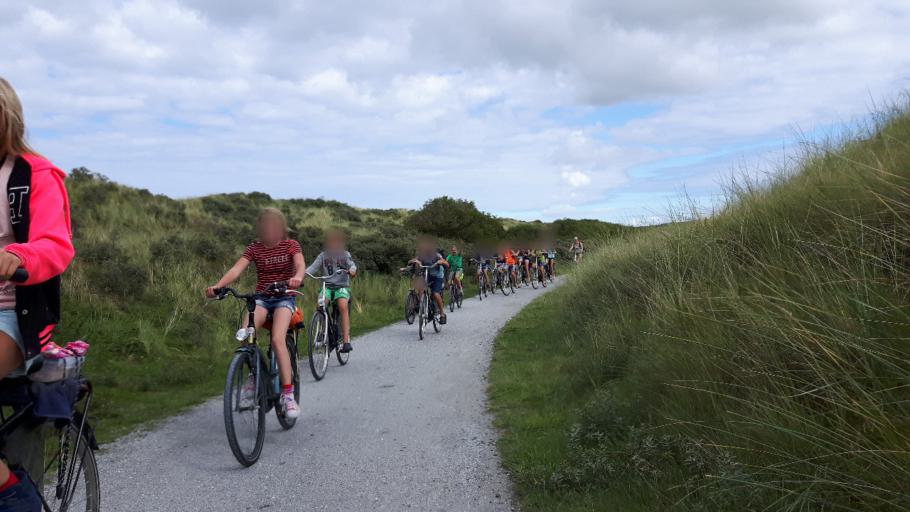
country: NL
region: Friesland
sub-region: Gemeente Ameland
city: Nes
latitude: 53.4579
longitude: 5.7205
